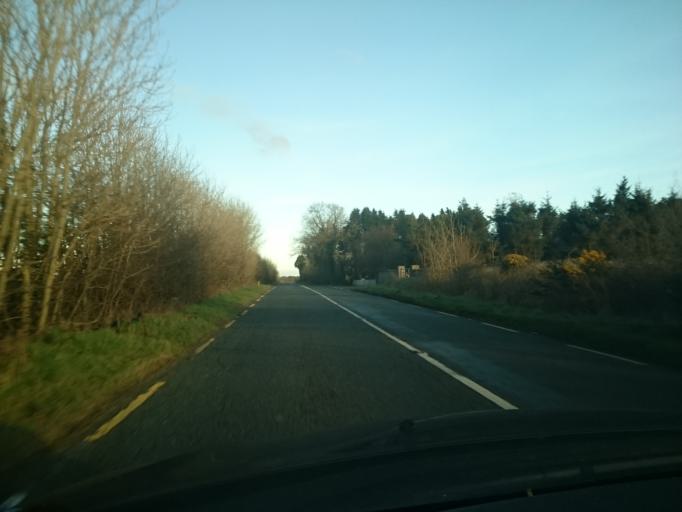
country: IE
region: Connaught
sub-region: Maigh Eo
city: Claremorris
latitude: 53.7726
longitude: -9.0620
